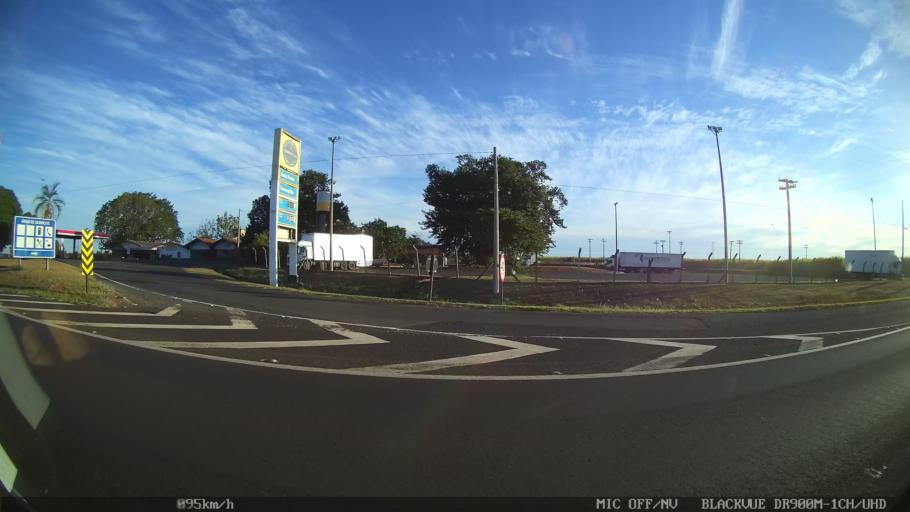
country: BR
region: Sao Paulo
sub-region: Urupes
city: Urupes
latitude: -21.0171
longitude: -49.1718
